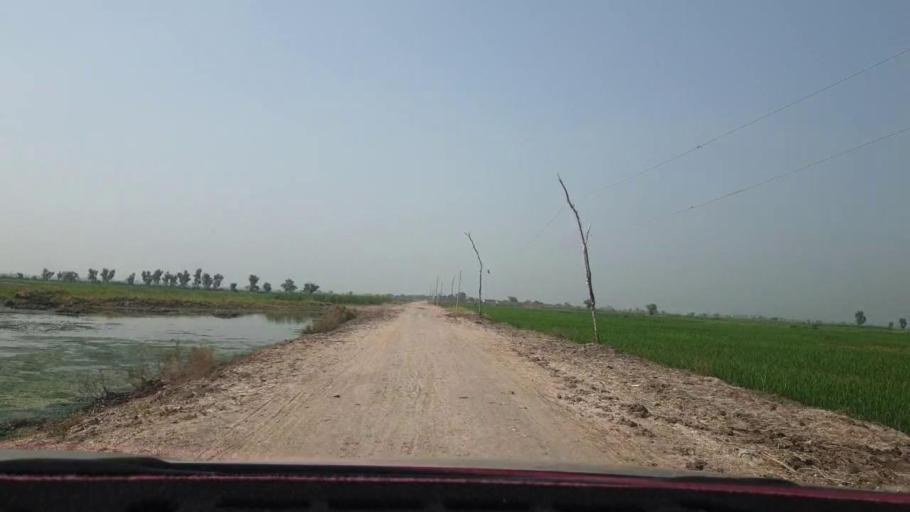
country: PK
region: Sindh
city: Nasirabad
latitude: 27.4344
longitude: 67.9558
